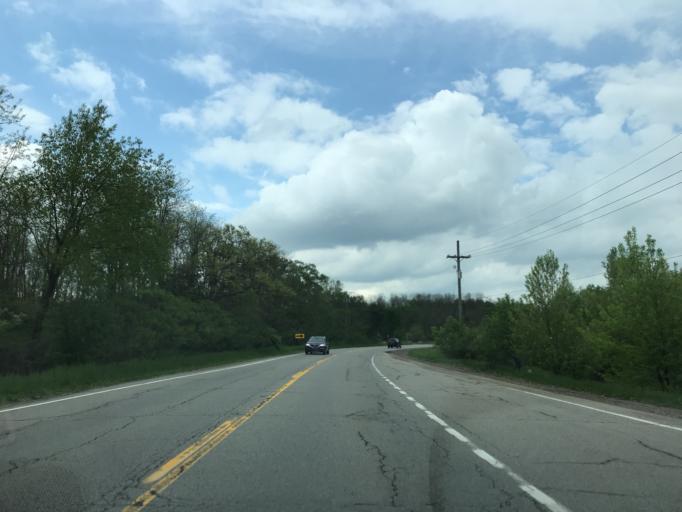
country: US
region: Michigan
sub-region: Oakland County
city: South Lyon
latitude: 42.5106
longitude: -83.6596
